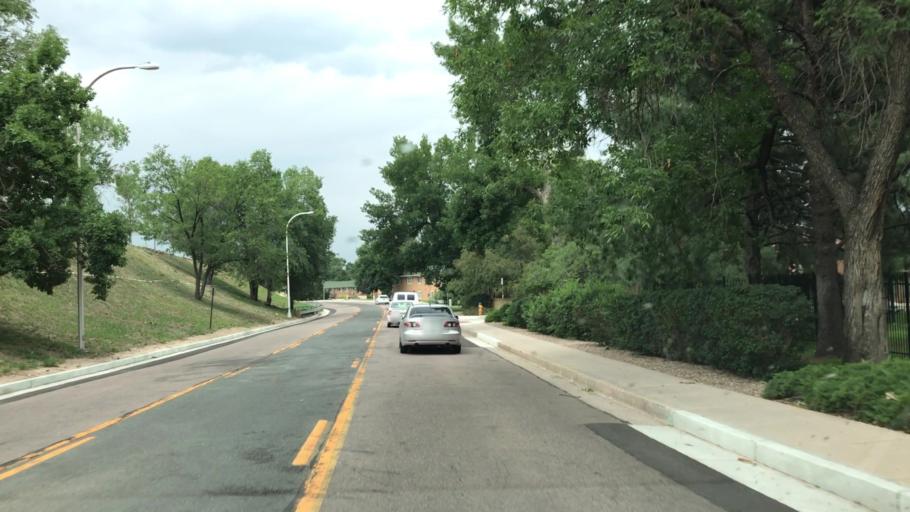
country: US
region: Colorado
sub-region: El Paso County
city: Colorado Springs
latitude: 38.8016
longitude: -104.8176
